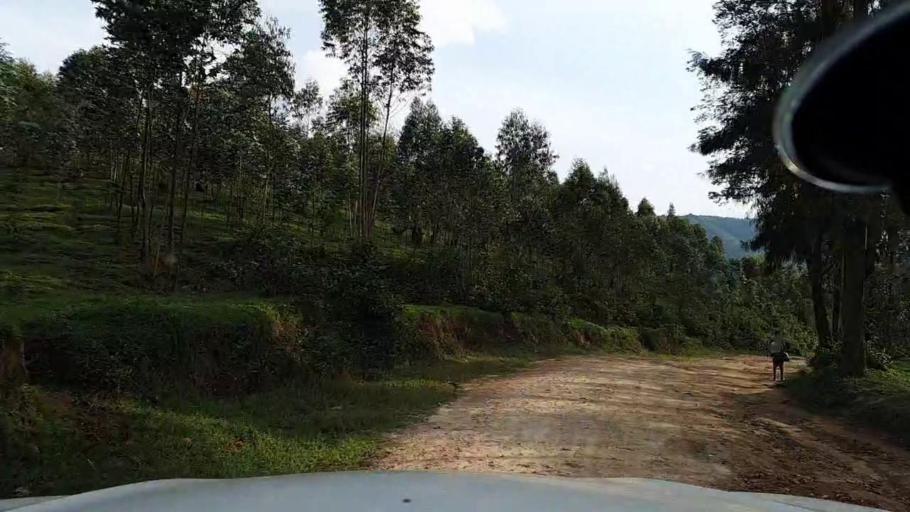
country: RW
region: Southern Province
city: Gitarama
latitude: -2.1942
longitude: 29.5799
